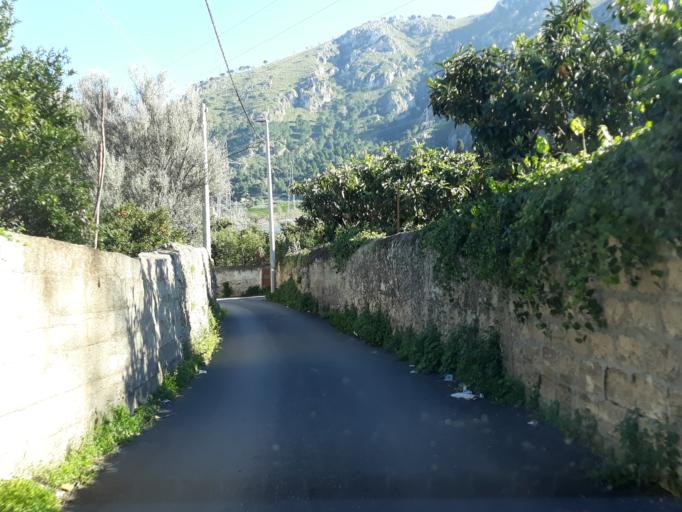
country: IT
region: Sicily
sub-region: Palermo
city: Villa Ciambra
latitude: 38.0755
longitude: 13.3602
